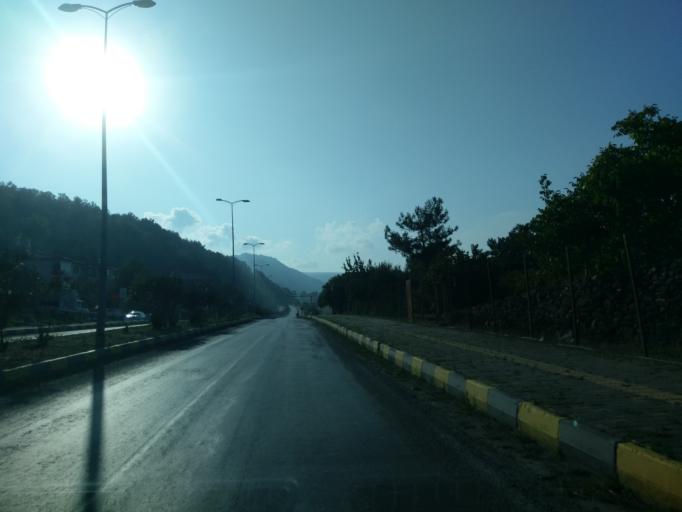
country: TR
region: Kastamonu
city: Catalzeytin
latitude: 41.9554
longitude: 34.2034
